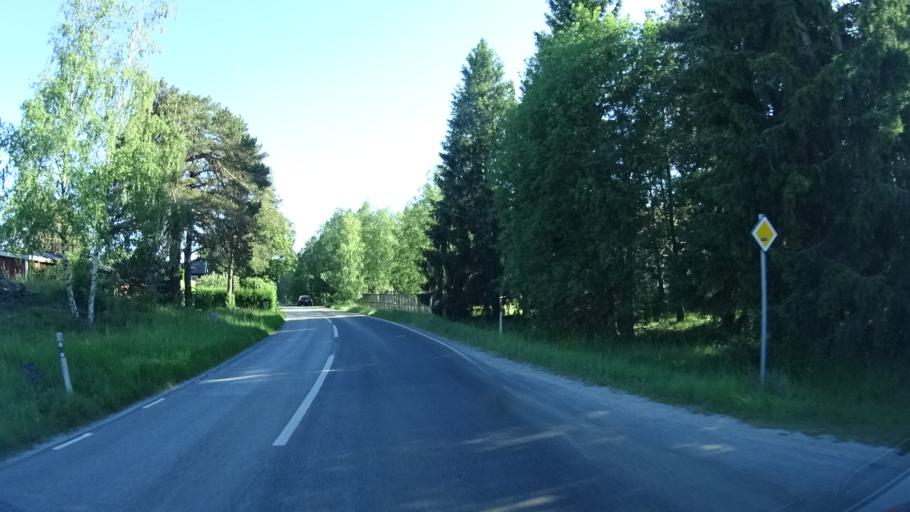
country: SE
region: Stockholm
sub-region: Vallentuna Kommun
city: Vallentuna
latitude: 59.5548
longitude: 18.1000
